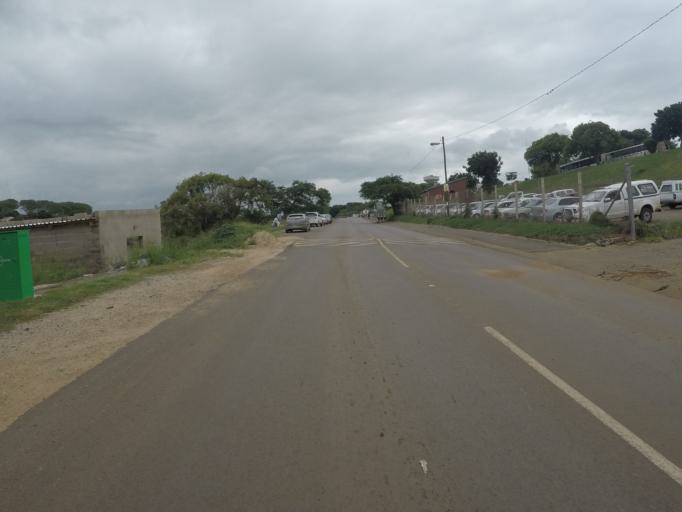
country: ZA
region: KwaZulu-Natal
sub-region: uThungulu District Municipality
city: Empangeni
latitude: -28.7786
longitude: 31.8640
